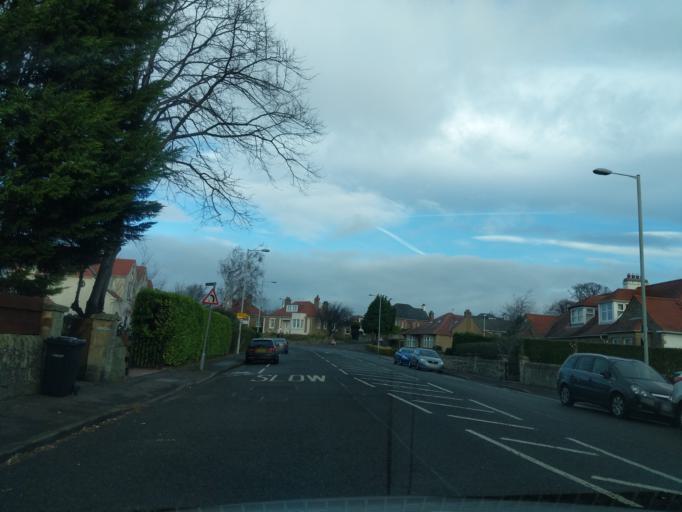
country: GB
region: Scotland
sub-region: Edinburgh
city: Colinton
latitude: 55.9622
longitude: -3.2641
